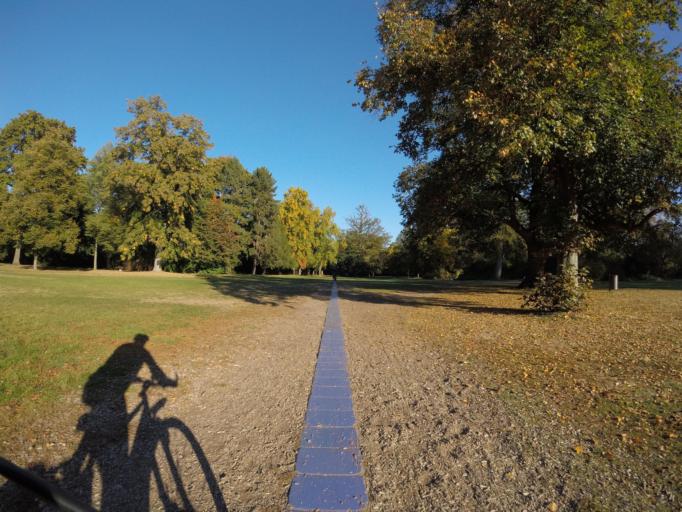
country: DE
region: Baden-Wuerttemberg
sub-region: Karlsruhe Region
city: Karlsruhe
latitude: 49.0153
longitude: 8.4038
